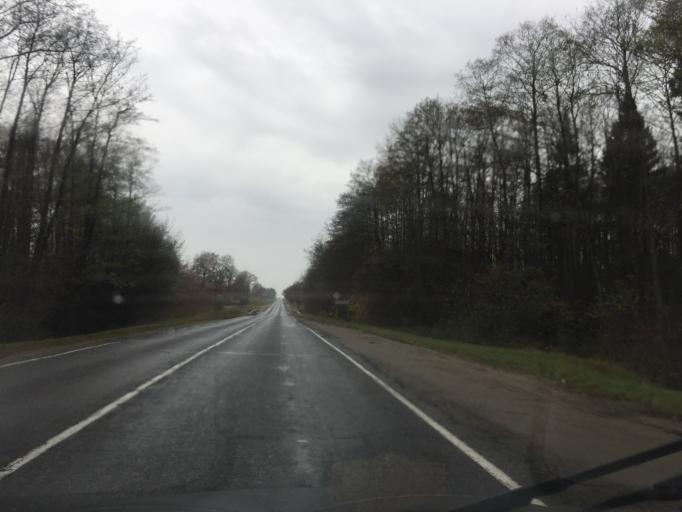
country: BY
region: Mogilev
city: Slawharad
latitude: 53.4069
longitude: 30.9345
